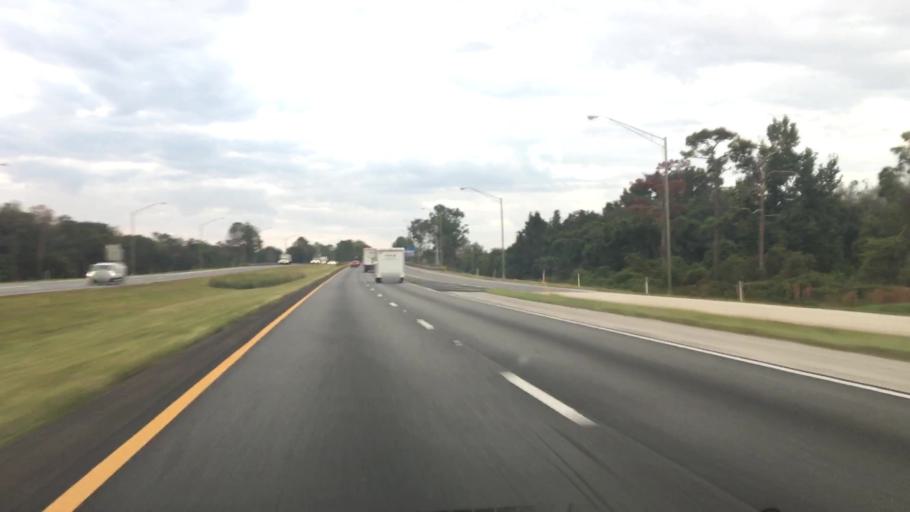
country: US
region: Florida
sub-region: Seminole County
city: Oviedo
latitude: 28.6857
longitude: -81.2270
